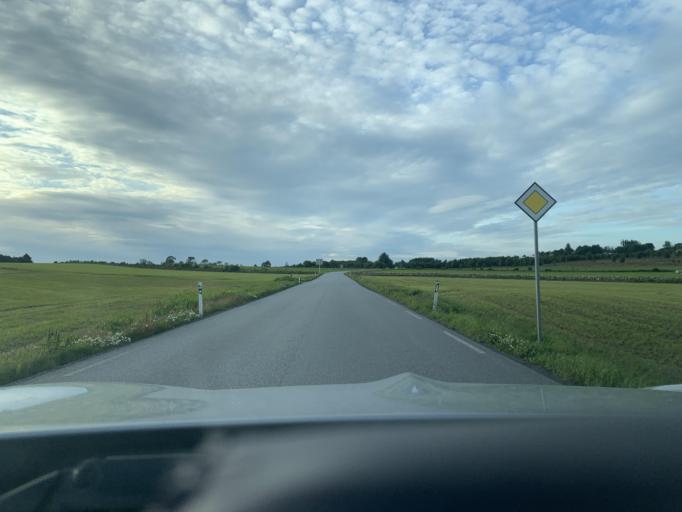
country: NO
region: Rogaland
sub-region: Time
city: Bryne
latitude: 58.6934
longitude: 5.7105
